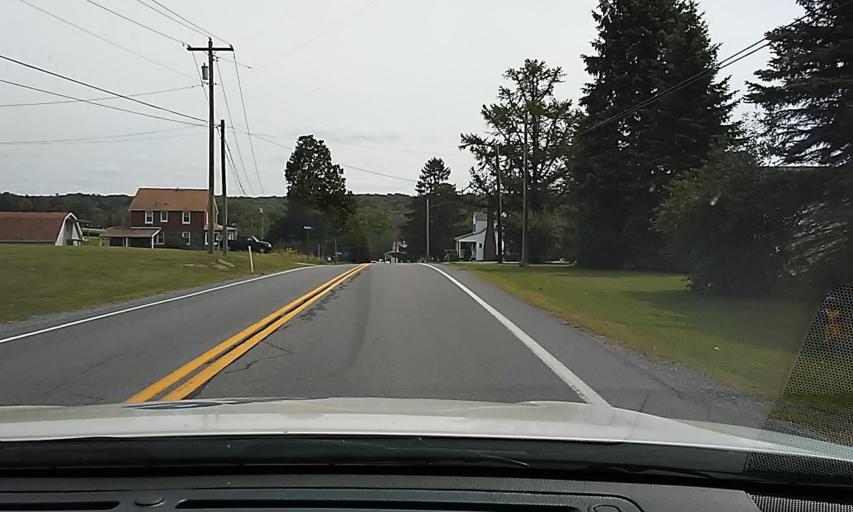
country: US
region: Pennsylvania
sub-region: Elk County
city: Saint Marys
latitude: 41.3611
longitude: -78.5703
